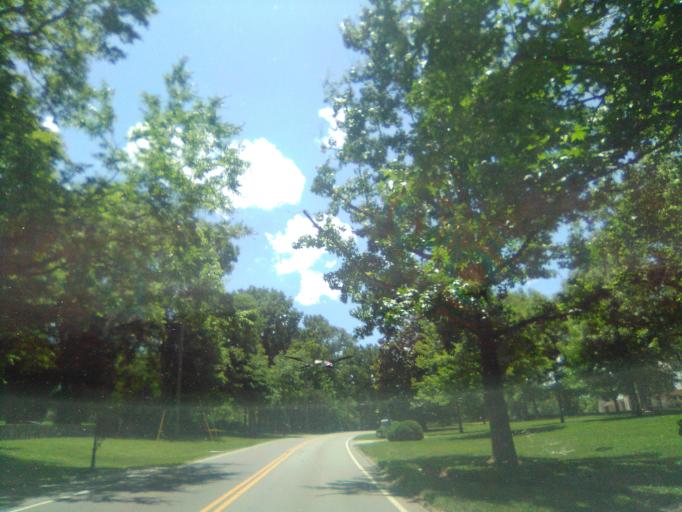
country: US
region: Tennessee
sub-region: Davidson County
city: Belle Meade
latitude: 36.1044
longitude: -86.8527
